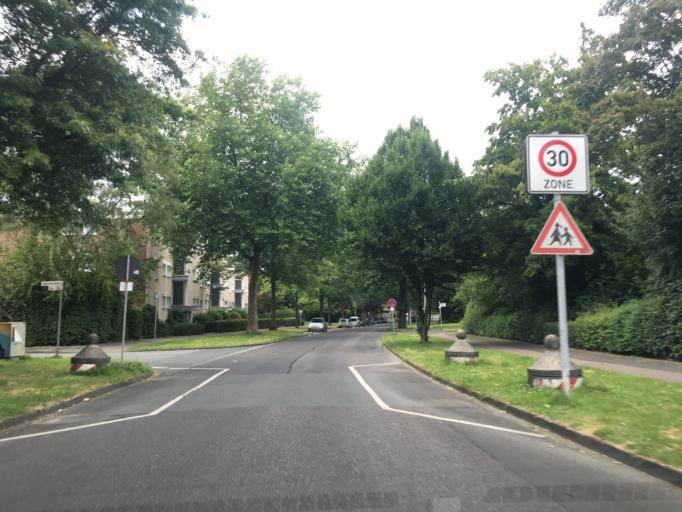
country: DE
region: North Rhine-Westphalia
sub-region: Regierungsbezirk Munster
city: Muenster
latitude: 51.9145
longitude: 7.6851
